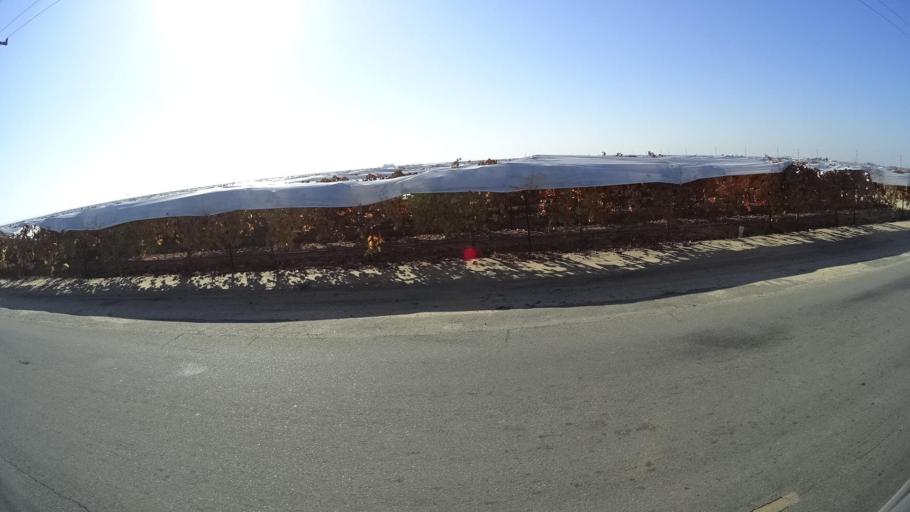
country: US
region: California
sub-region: Kern County
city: Delano
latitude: 35.7469
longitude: -119.2004
